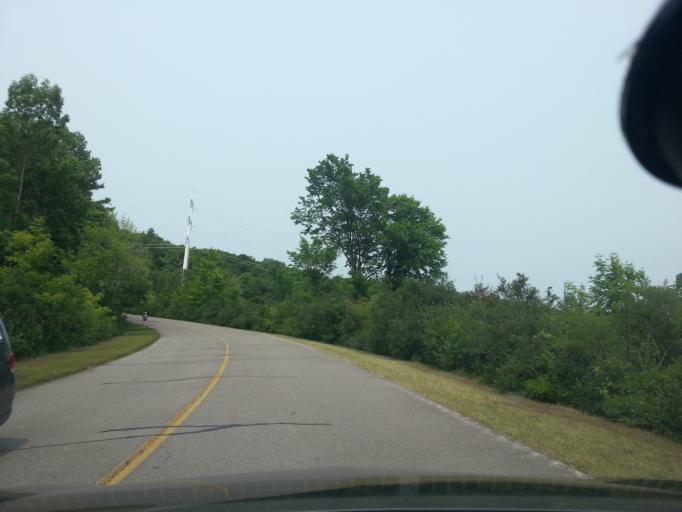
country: CA
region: Quebec
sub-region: Outaouais
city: Gatineau
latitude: 45.4672
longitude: -75.7914
